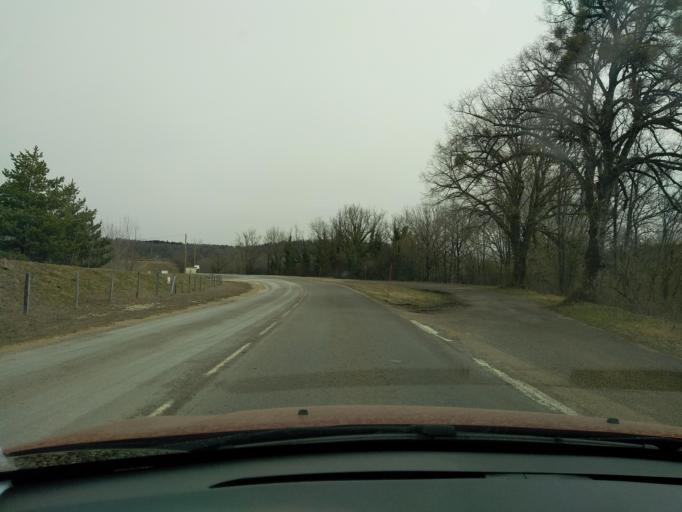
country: FR
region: Franche-Comte
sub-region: Departement du Jura
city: Clairvaux-les-Lacs
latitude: 46.6191
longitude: 5.7428
